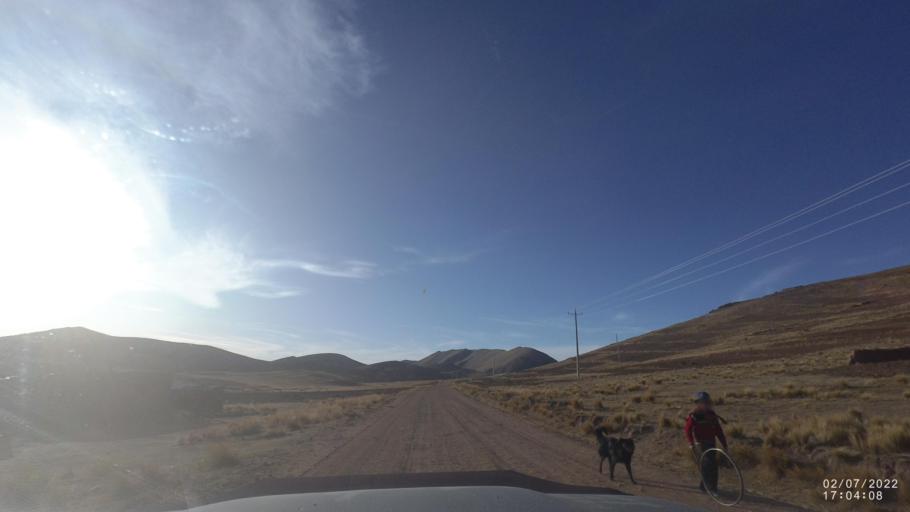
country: BO
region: Cochabamba
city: Irpa Irpa
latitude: -17.9180
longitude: -66.5581
